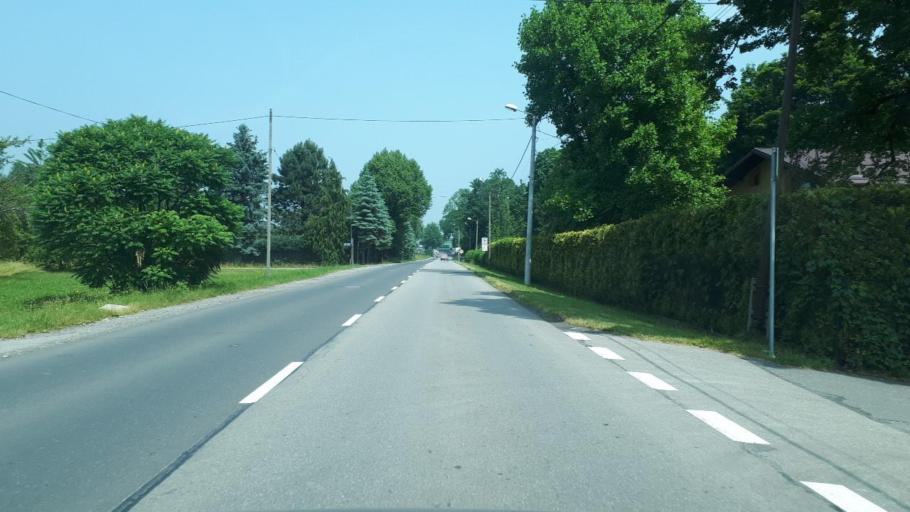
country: PL
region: Silesian Voivodeship
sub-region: Powiat cieszynski
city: Ustron
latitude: 49.7494
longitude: 18.8047
